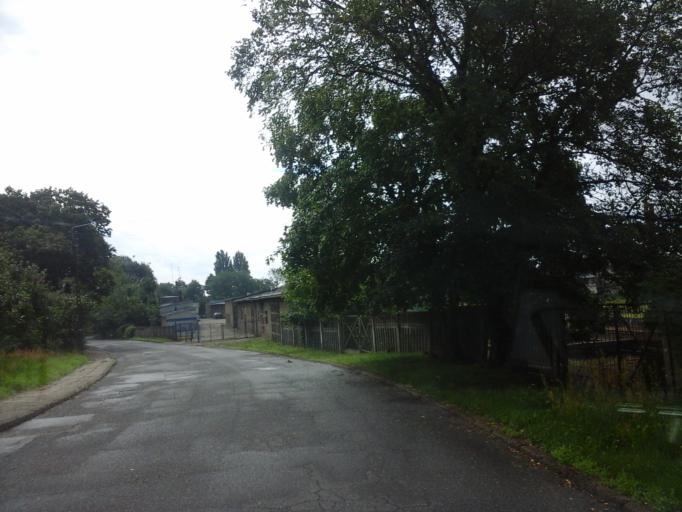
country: PL
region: West Pomeranian Voivodeship
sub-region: Powiat choszczenski
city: Choszczno
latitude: 53.1638
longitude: 15.4067
